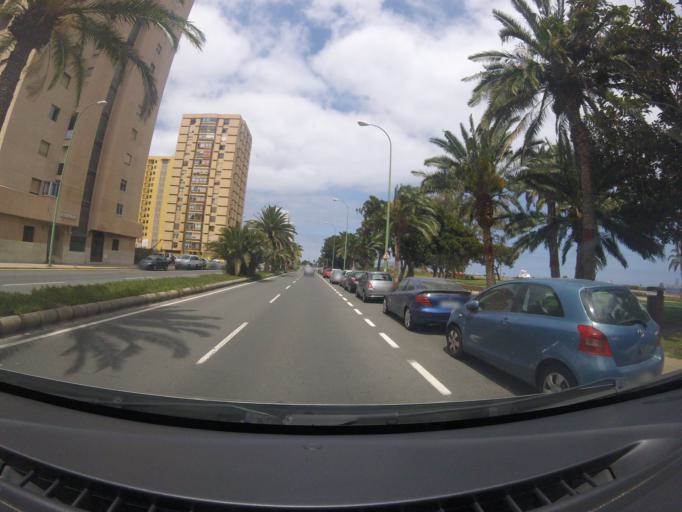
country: ES
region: Canary Islands
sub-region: Provincia de Las Palmas
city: Las Palmas de Gran Canaria
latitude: 28.0893
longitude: -15.4159
